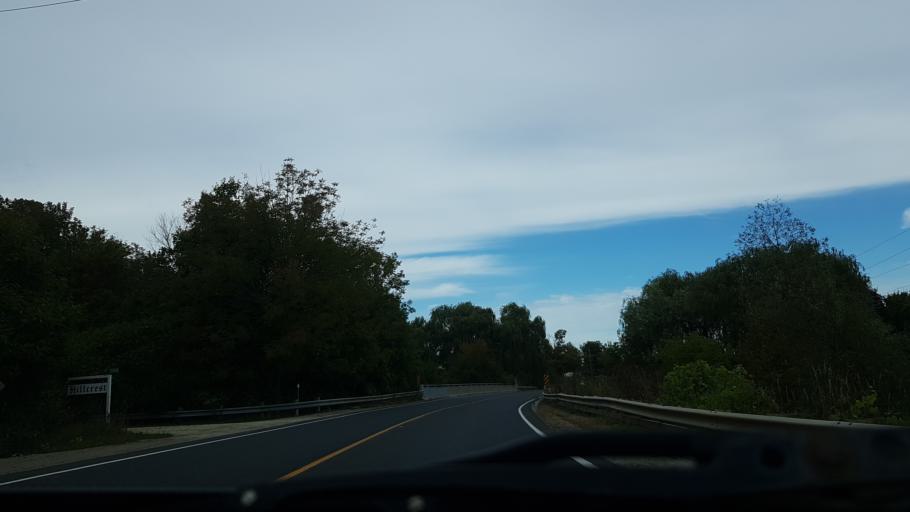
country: CA
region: Ontario
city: Angus
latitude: 44.3061
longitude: -80.0717
